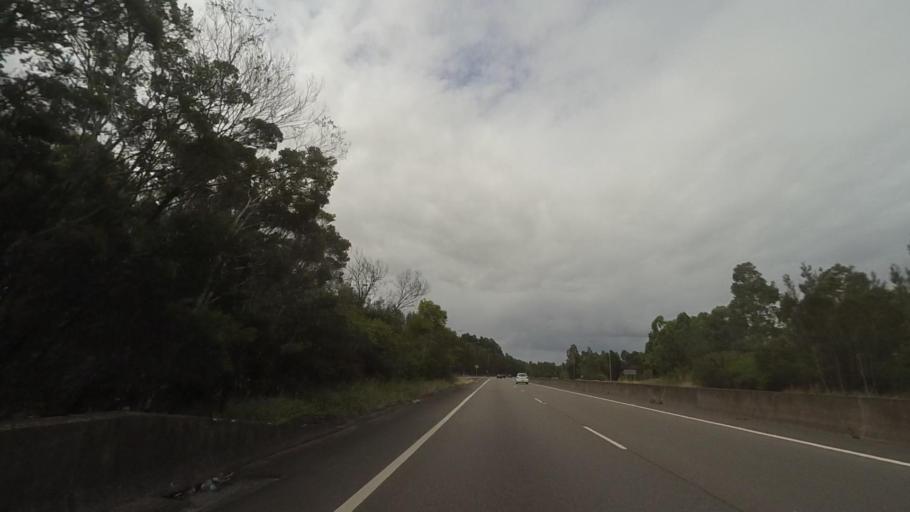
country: AU
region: New South Wales
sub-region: Port Stephens Shire
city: Raymond Terrace
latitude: -32.7529
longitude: 151.7661
